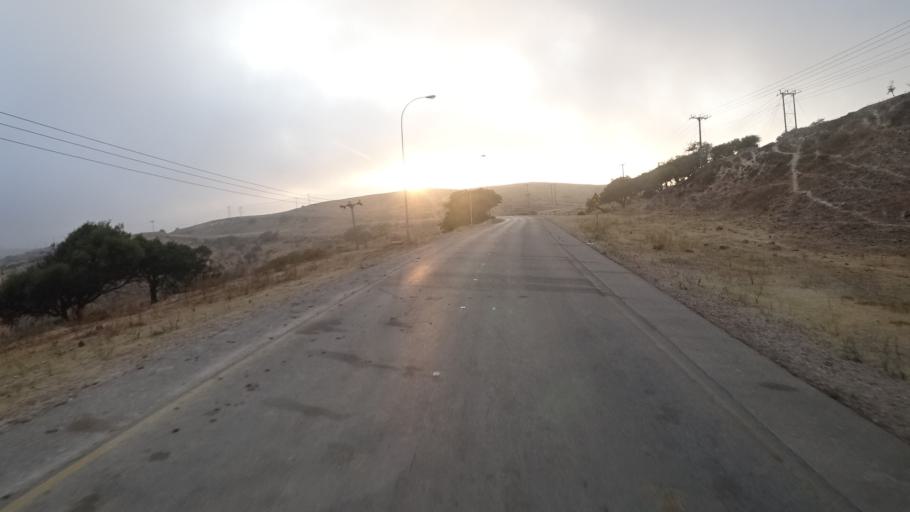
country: OM
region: Zufar
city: Salalah
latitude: 17.1363
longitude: 53.9655
